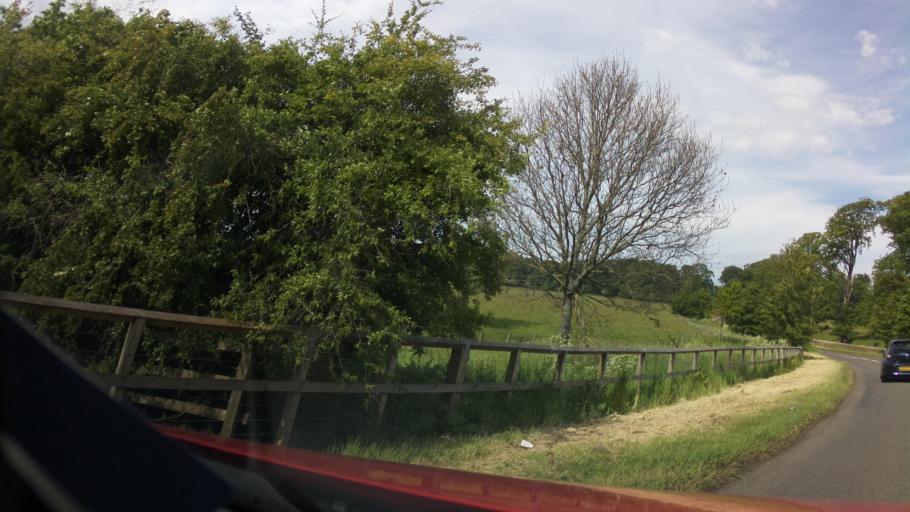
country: GB
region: England
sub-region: Northumberland
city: Alnwick
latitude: 55.4229
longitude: -1.7044
